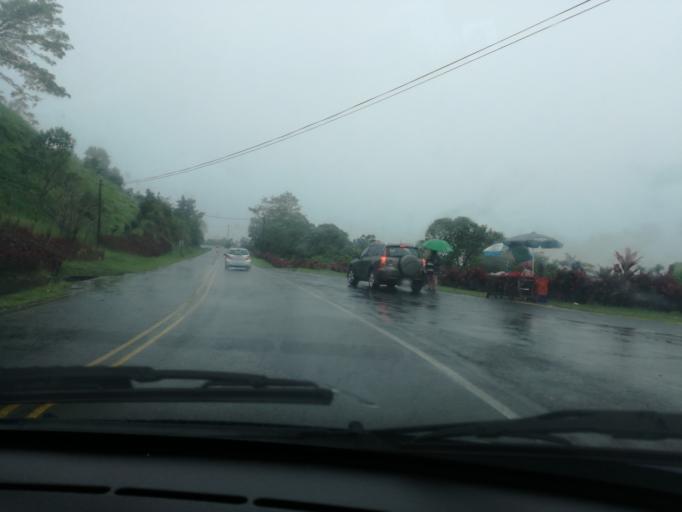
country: CR
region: Cartago
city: Tucurrique
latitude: 9.8954
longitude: -83.7855
